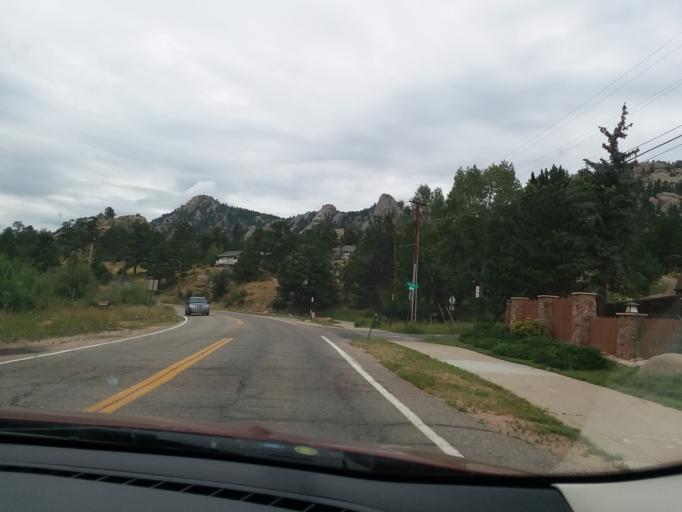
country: US
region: Colorado
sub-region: Larimer County
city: Estes Park
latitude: 40.3780
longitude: -105.5327
